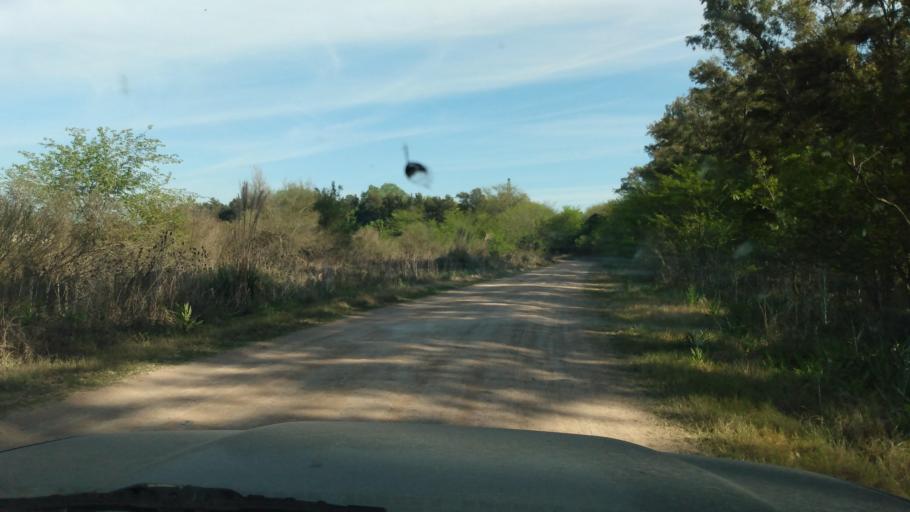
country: AR
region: Buenos Aires
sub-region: Partido de Lujan
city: Lujan
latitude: -34.6297
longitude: -59.1045
